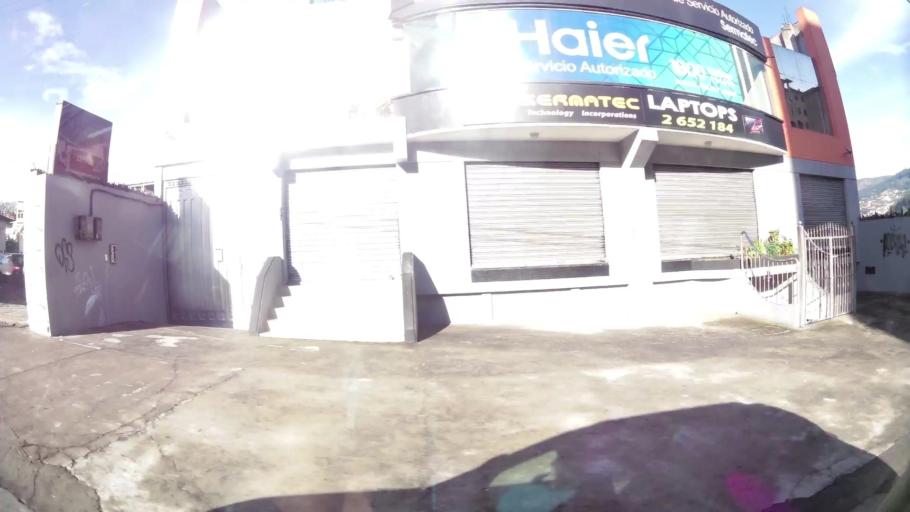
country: EC
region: Pichincha
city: Quito
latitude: -0.2371
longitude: -78.5099
